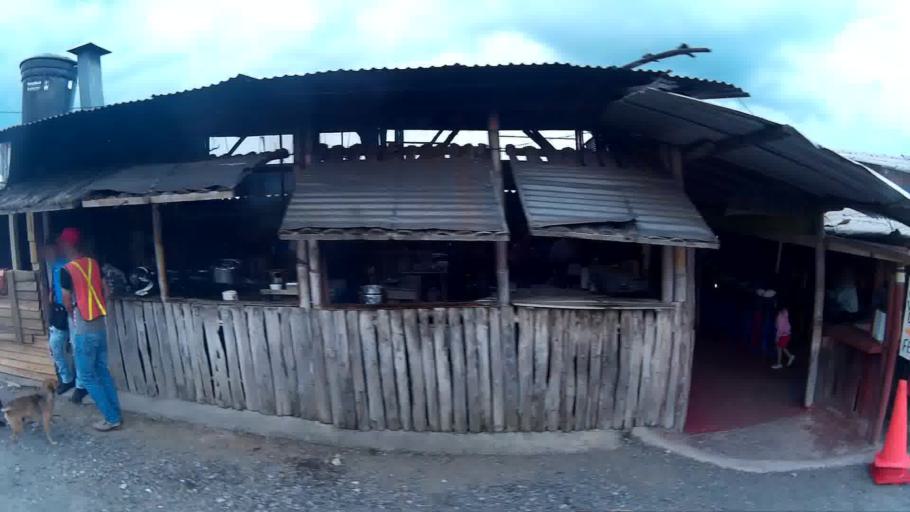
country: CO
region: Valle del Cauca
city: Ulloa
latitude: 4.7579
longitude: -75.7174
